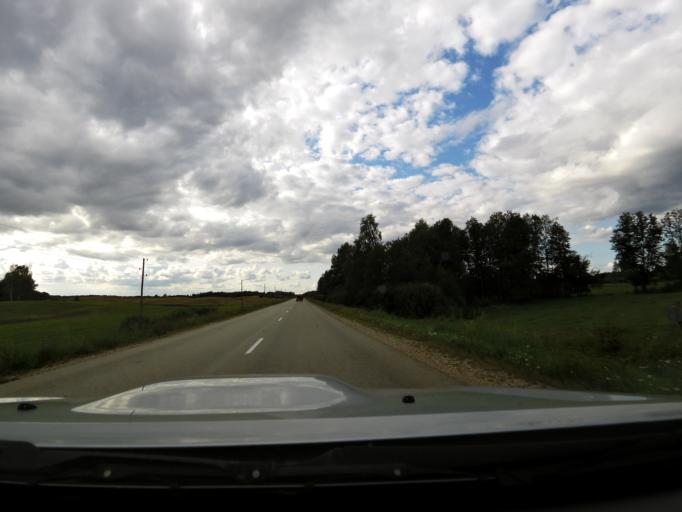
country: LV
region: Akniste
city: Akniste
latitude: 55.9864
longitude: 25.9863
